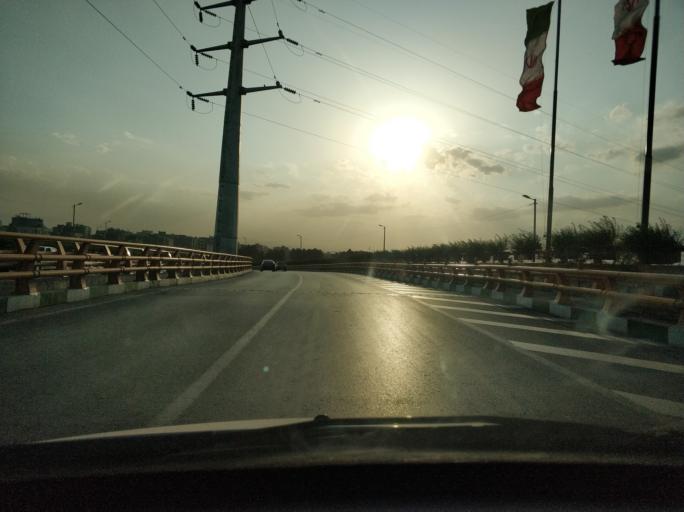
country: IR
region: Razavi Khorasan
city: Mashhad
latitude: 36.3401
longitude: 59.5469
